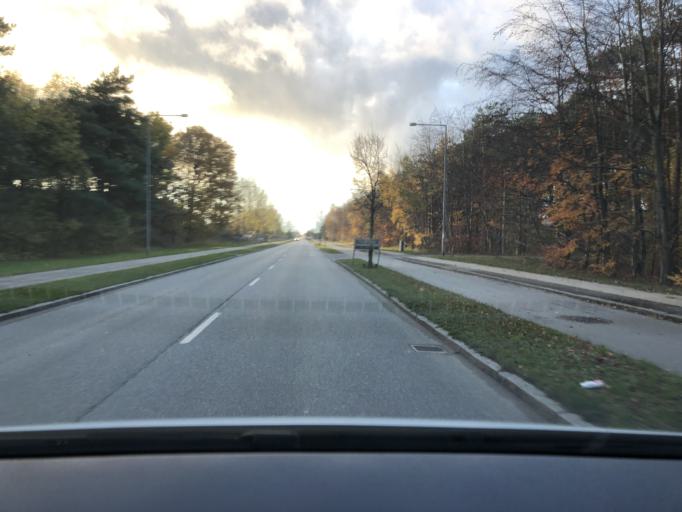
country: DK
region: Capital Region
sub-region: Tarnby Kommune
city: Tarnby
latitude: 55.6056
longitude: 12.5951
